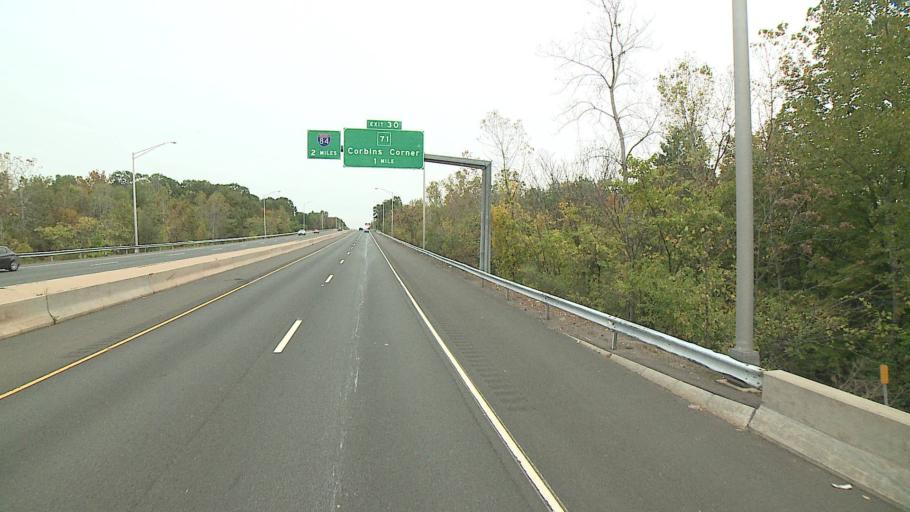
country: US
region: Connecticut
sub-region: Hartford County
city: Newington
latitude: 41.6955
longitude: -72.7580
